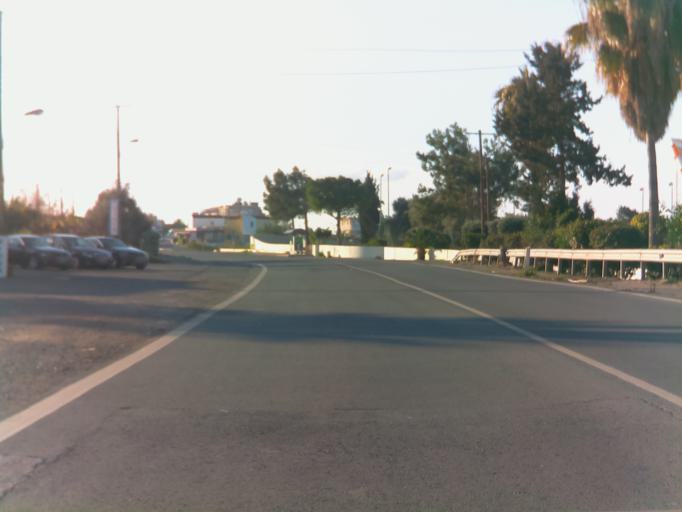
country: CY
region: Pafos
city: Kissonerga
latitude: 34.8066
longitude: 32.3969
